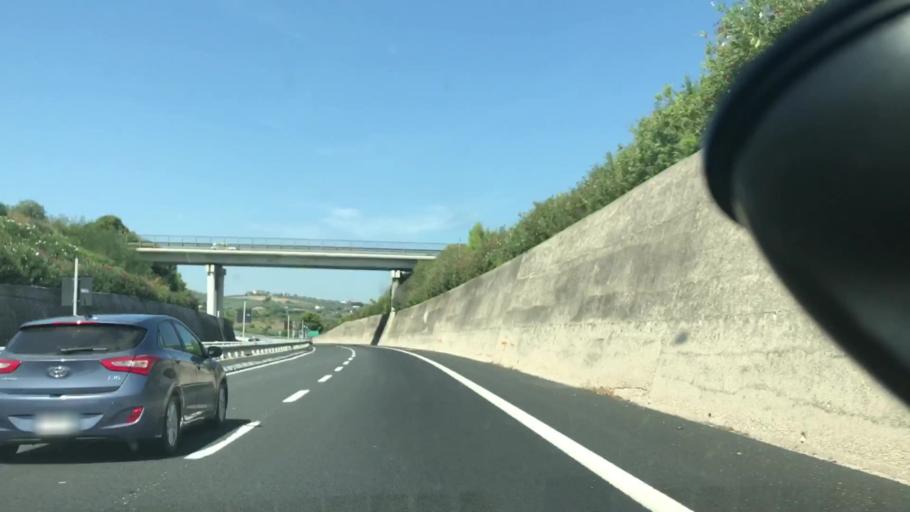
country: IT
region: Abruzzo
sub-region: Provincia di Chieti
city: San Salvo
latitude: 42.0598
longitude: 14.7420
